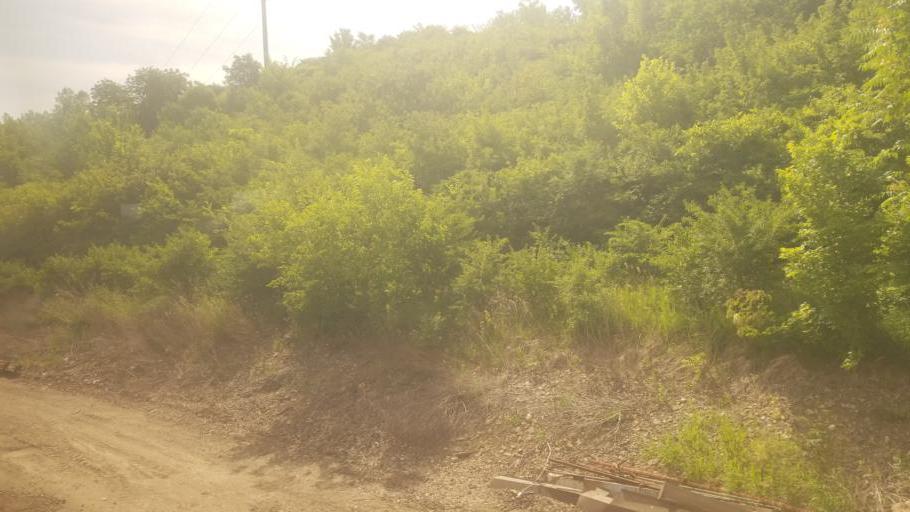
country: US
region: Missouri
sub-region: Jackson County
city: Kansas City
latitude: 39.0810
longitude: -94.6105
